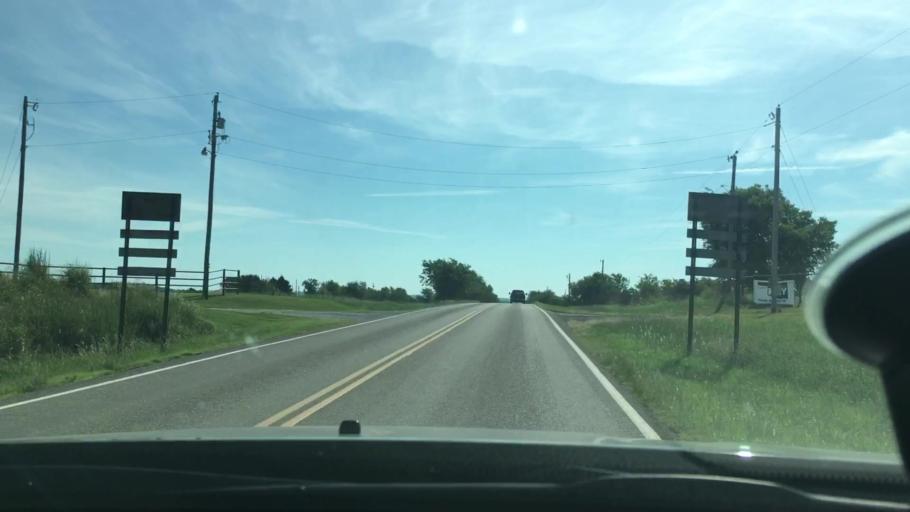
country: US
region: Oklahoma
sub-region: Carter County
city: Lone Grove
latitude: 34.3327
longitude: -97.2226
